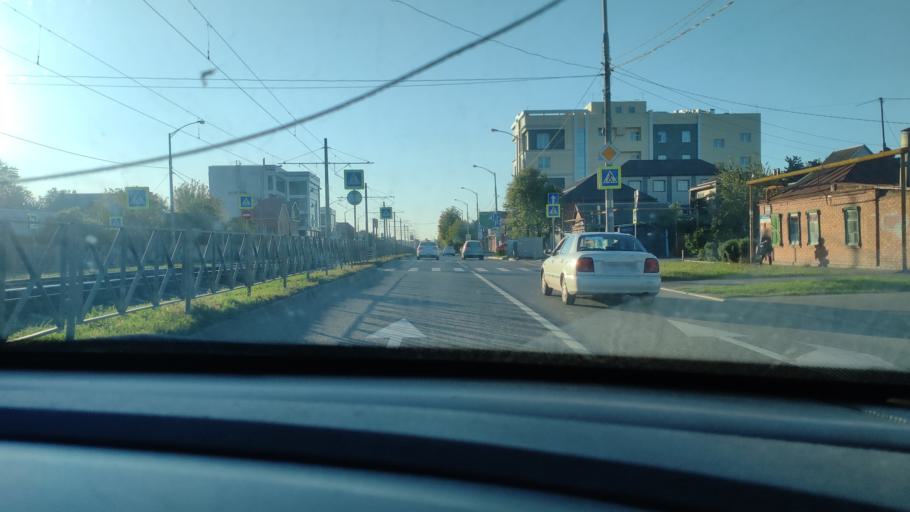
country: RU
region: Krasnodarskiy
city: Krasnodar
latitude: 45.0407
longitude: 38.9519
